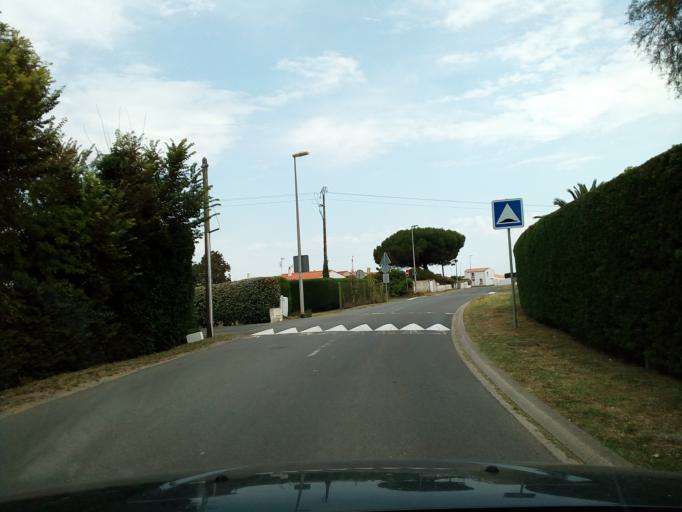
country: FR
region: Poitou-Charentes
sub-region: Departement de la Charente-Maritime
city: Dolus-d'Oleron
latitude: 45.9459
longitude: -1.2996
